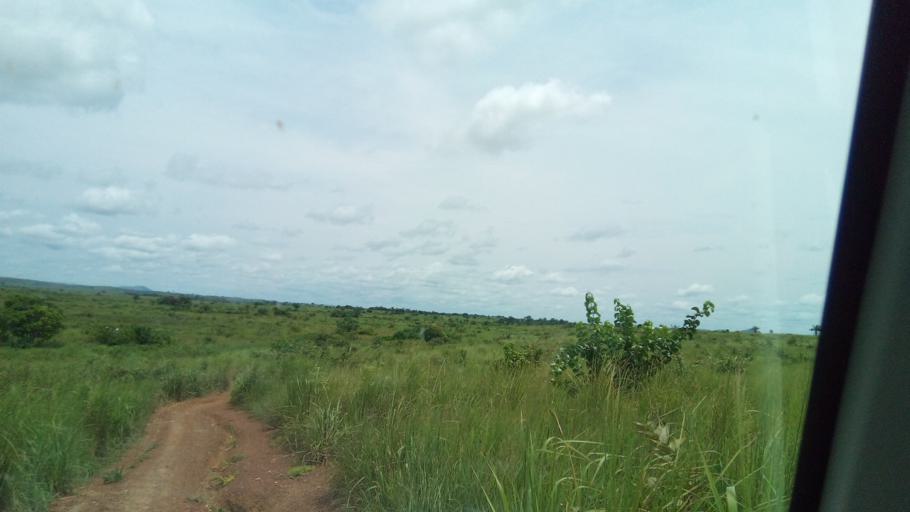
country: AO
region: Zaire
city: Mbanza Congo
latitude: -5.7854
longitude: 13.9916
